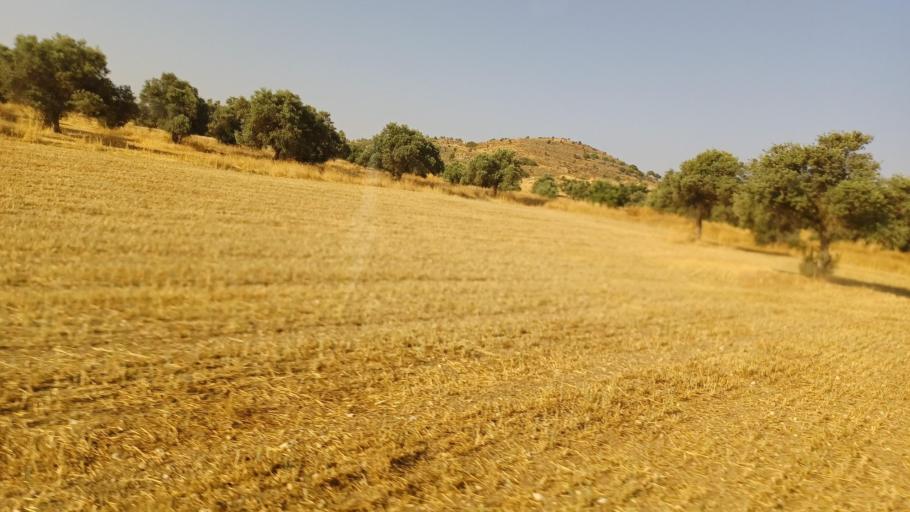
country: CY
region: Lefkosia
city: Lympia
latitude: 34.9959
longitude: 33.4336
